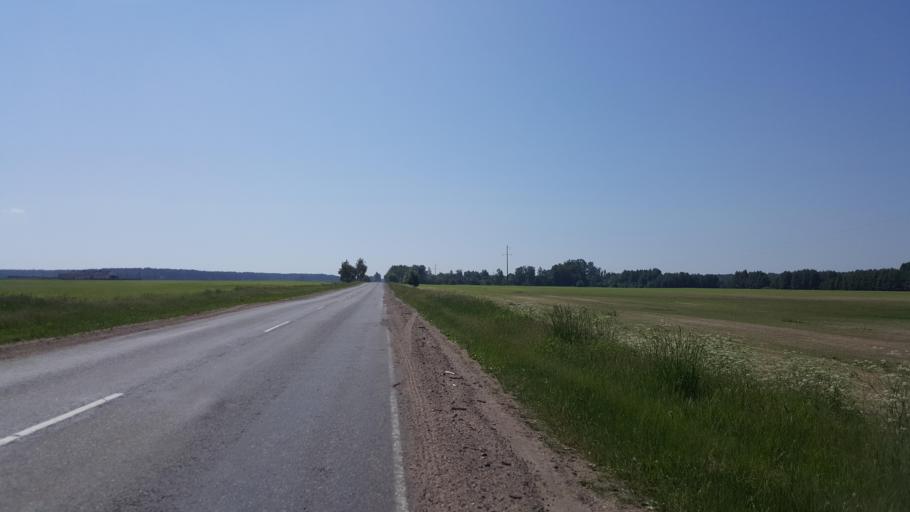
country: BY
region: Brest
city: Zhabinka
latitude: 52.2620
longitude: 23.9617
